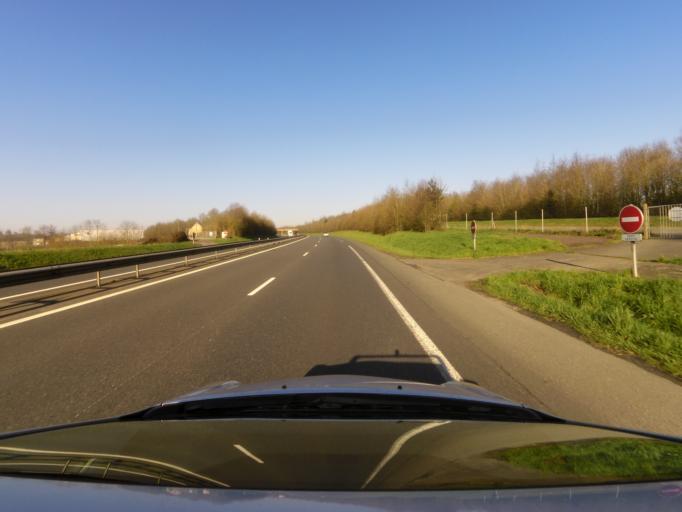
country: FR
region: Lower Normandy
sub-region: Departement du Calvados
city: Cahagnes
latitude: 49.0508
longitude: -0.7436
